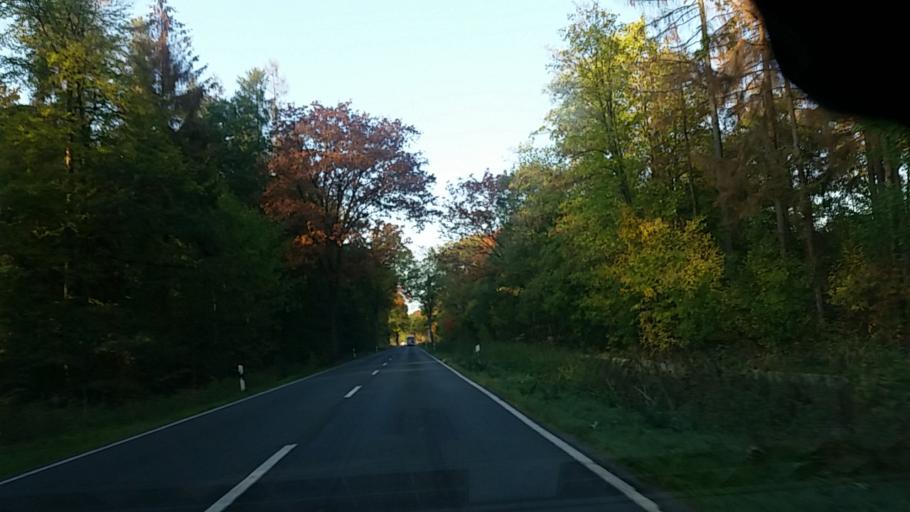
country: DE
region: Lower Saxony
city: Wolfsburg
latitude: 52.3763
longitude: 10.7434
